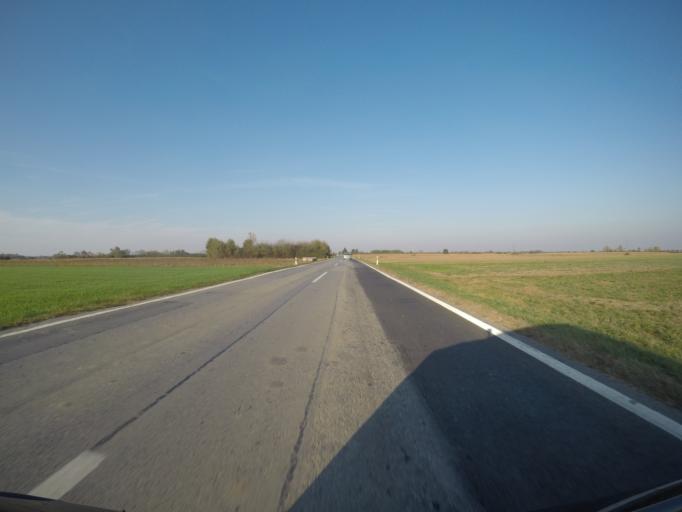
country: HU
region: Somogy
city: Barcs
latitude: 45.9179
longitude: 17.4496
